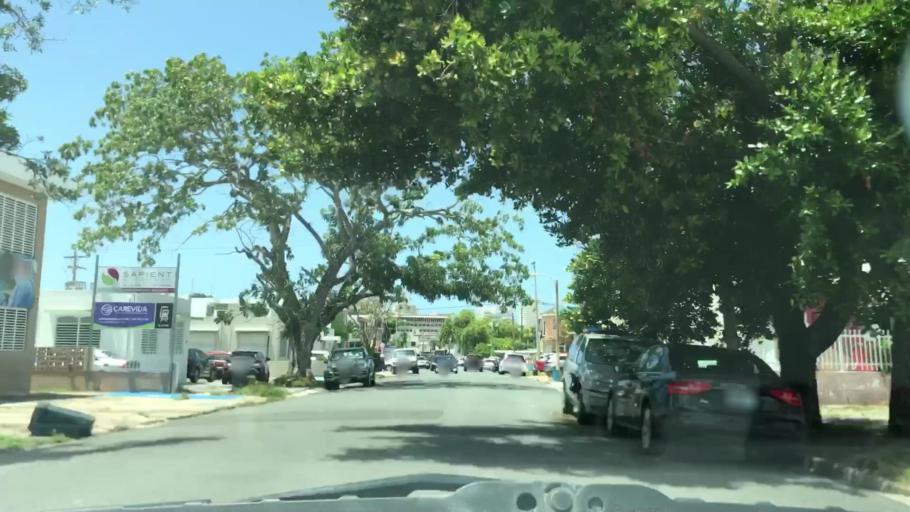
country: PR
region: Catano
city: Catano
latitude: 18.4178
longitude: -66.0623
